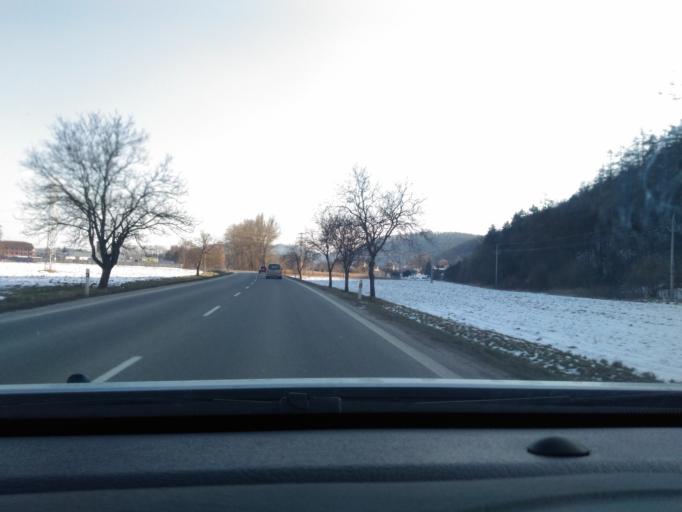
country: CZ
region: South Moravian
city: Tisnov
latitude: 49.3456
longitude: 16.4130
